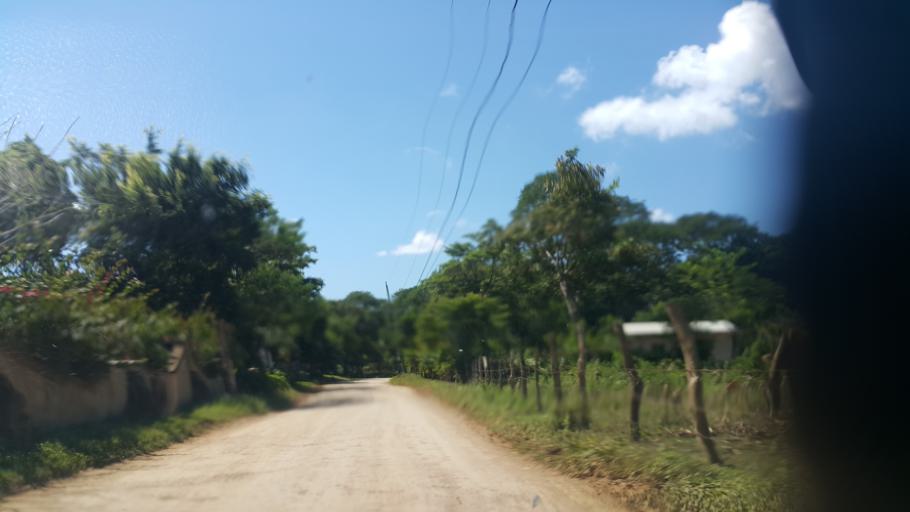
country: NI
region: Rivas
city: San Juan del Sur
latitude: 11.2965
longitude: -85.8899
